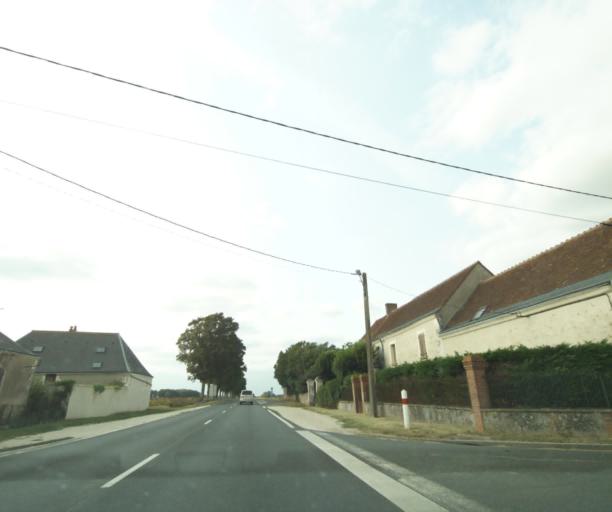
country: FR
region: Centre
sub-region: Departement d'Indre-et-Loire
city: Truyes
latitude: 47.2373
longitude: 0.8671
